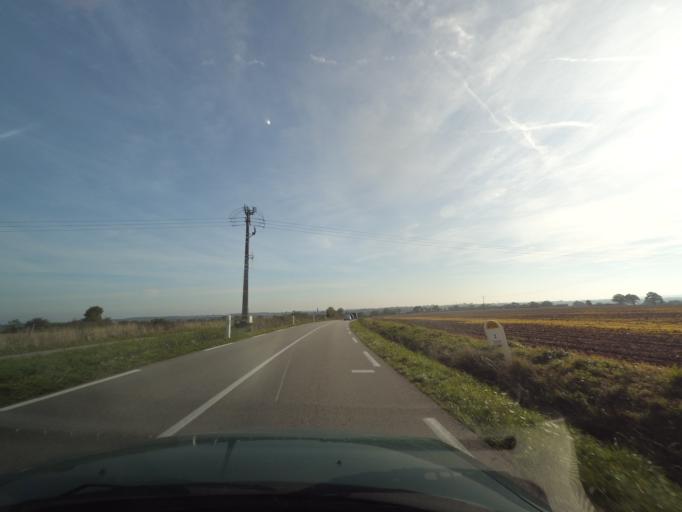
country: FR
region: Pays de la Loire
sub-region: Departement de la Vendee
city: Tiffauges
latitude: 47.0087
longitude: -1.1345
